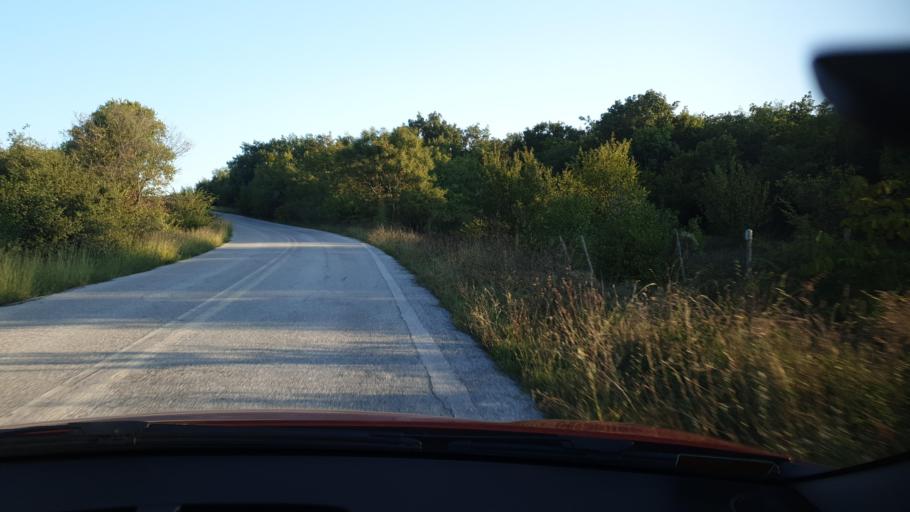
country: GR
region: Central Macedonia
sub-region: Nomos Chalkidikis
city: Galatista
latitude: 40.5479
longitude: 23.2835
